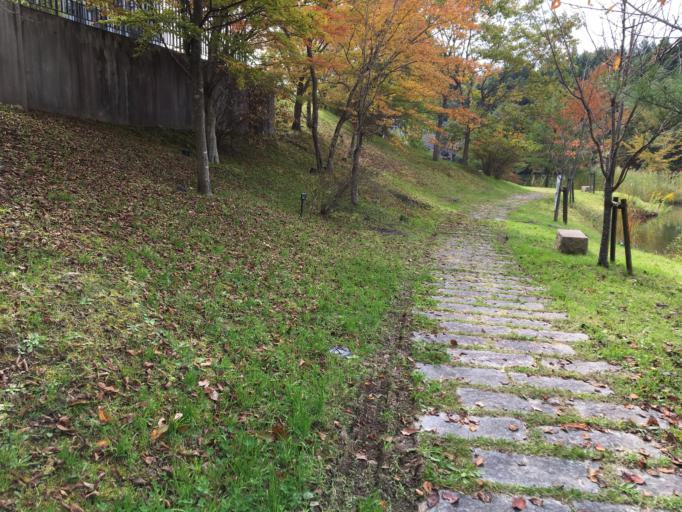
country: JP
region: Miyagi
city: Tomiya
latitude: 38.3504
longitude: 140.8411
